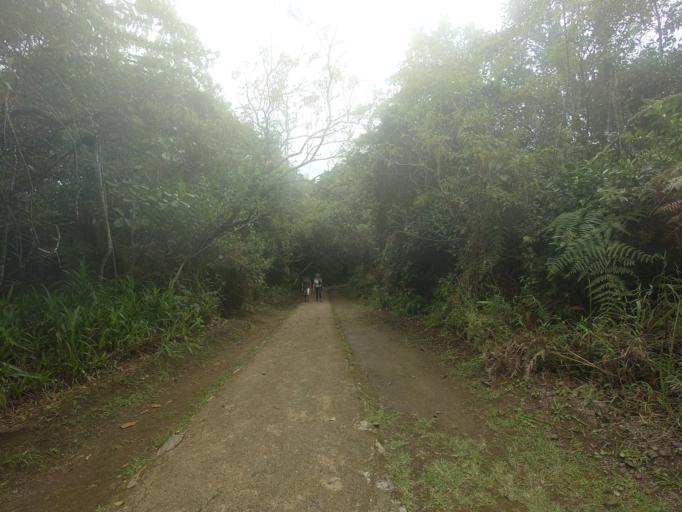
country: CO
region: Huila
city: San Agustin
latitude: 1.8811
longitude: -76.3009
